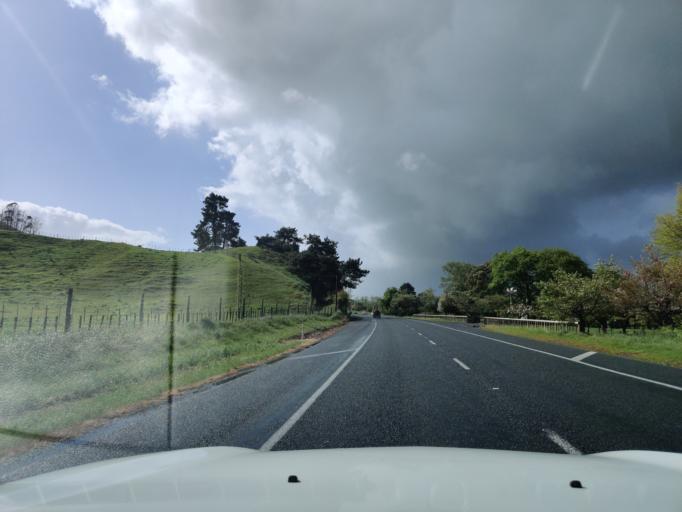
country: NZ
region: Waikato
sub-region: Waipa District
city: Cambridge
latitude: -37.9226
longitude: 175.5617
